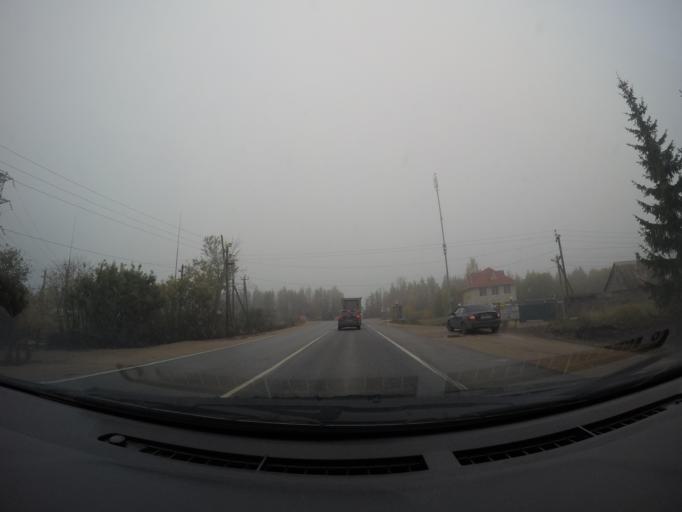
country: RU
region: Moskovskaya
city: Rumyantsevo
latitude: 55.8783
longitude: 36.5667
